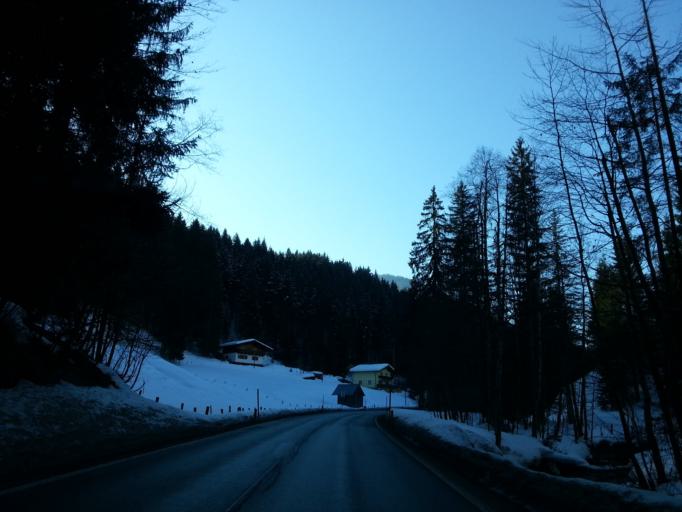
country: AT
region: Salzburg
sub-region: Politischer Bezirk Hallein
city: Abtenau
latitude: 47.4899
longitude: 13.3966
